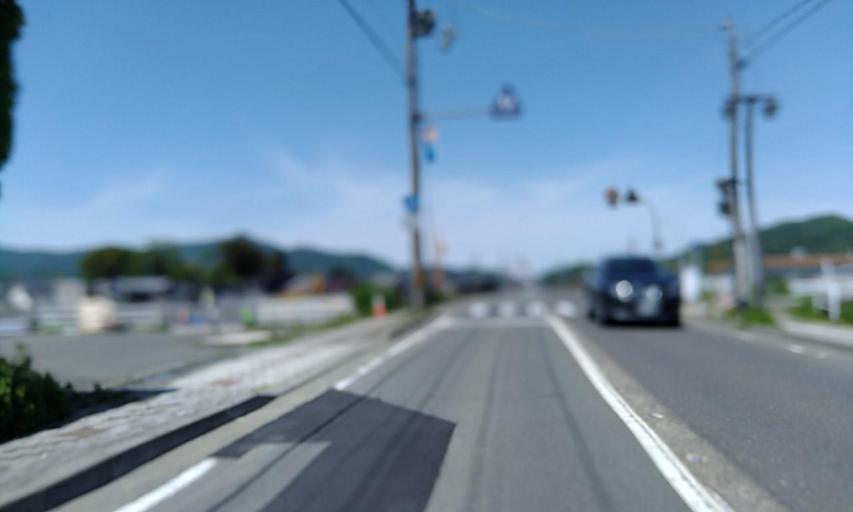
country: JP
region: Fukui
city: Obama
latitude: 35.5018
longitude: 135.7467
